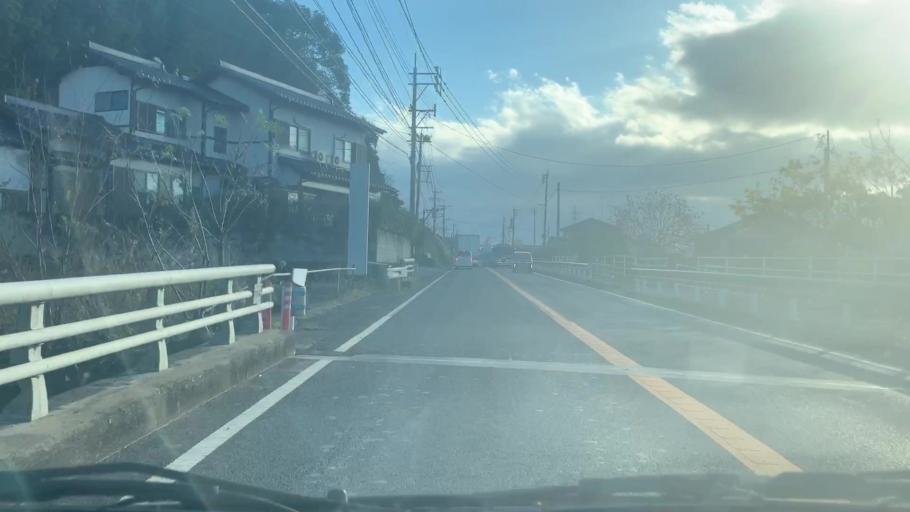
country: JP
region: Saga Prefecture
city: Takeocho-takeo
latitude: 33.2155
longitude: 130.0902
